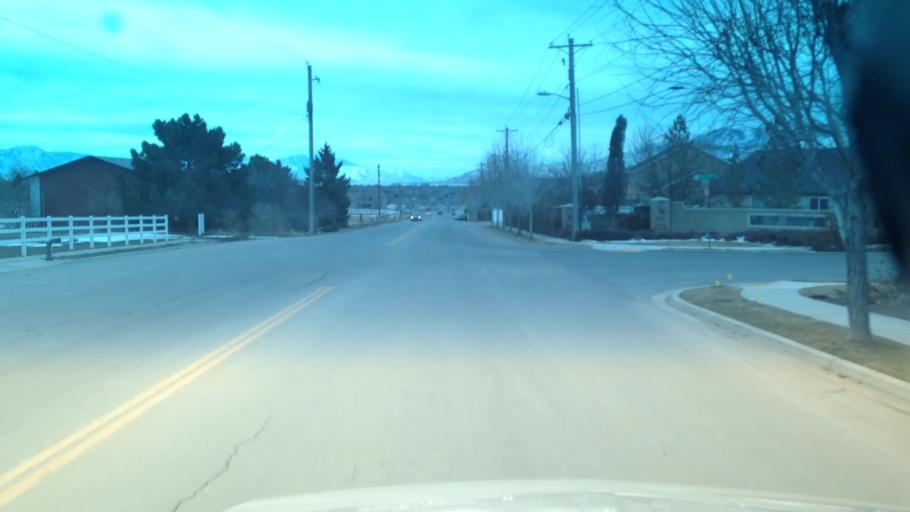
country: US
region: Utah
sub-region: Utah County
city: Lehi
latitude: 40.4262
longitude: -111.8689
